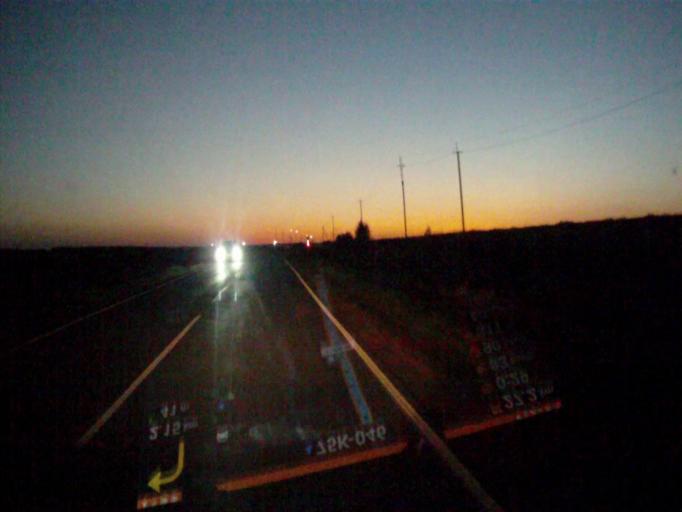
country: RU
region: Chelyabinsk
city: Chebarkul'
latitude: 55.2223
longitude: 60.4825
